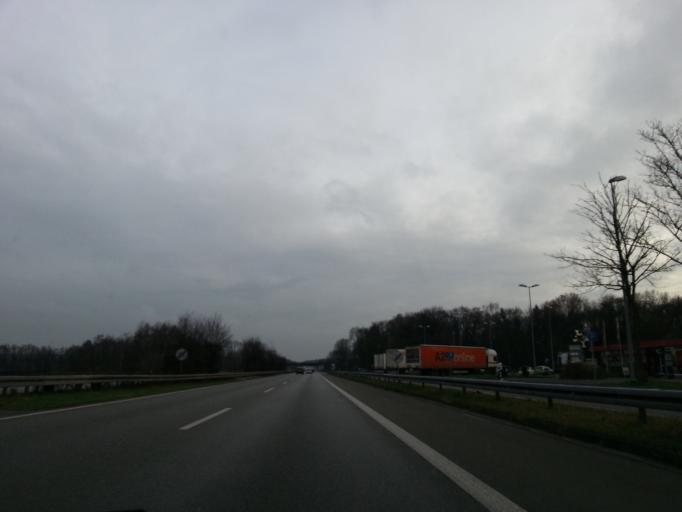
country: NL
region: Gelderland
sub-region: Gemeente Montferland
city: s-Heerenberg
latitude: 51.8980
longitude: 6.1661
